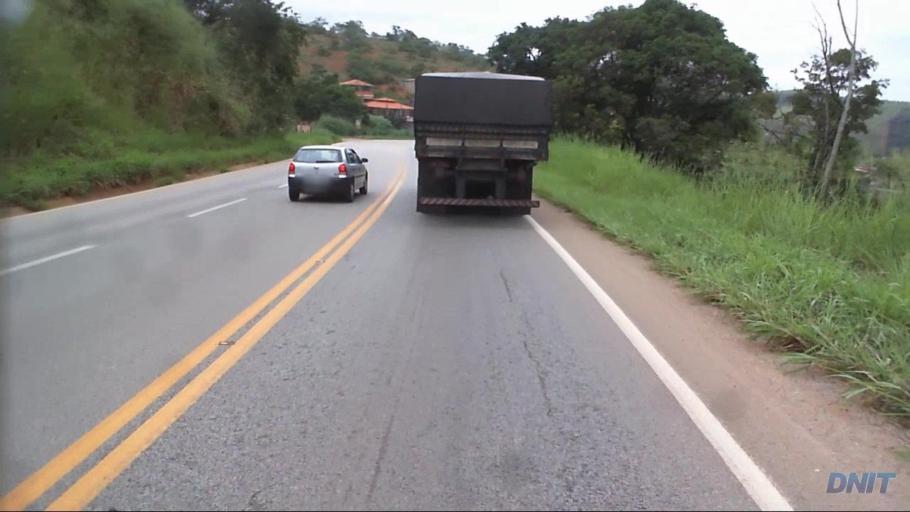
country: BR
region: Minas Gerais
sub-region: Nova Era
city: Nova Era
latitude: -19.8152
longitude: -43.0667
